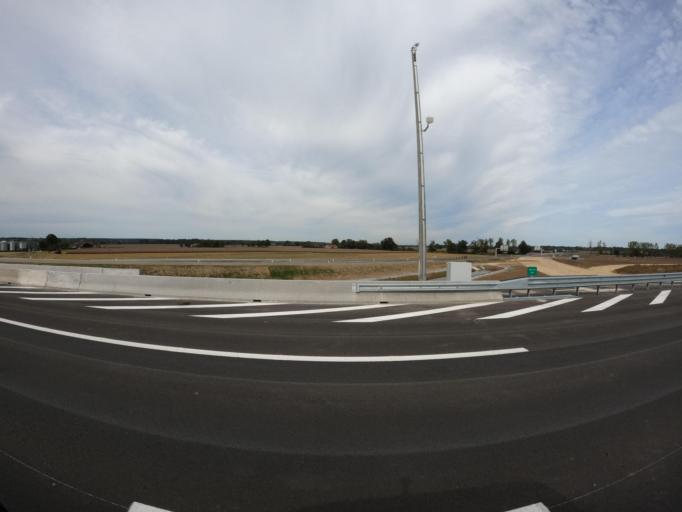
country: FR
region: Auvergne
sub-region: Departement de l'Allier
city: Toulon-sur-Allier
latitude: 46.4926
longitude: 3.3536
